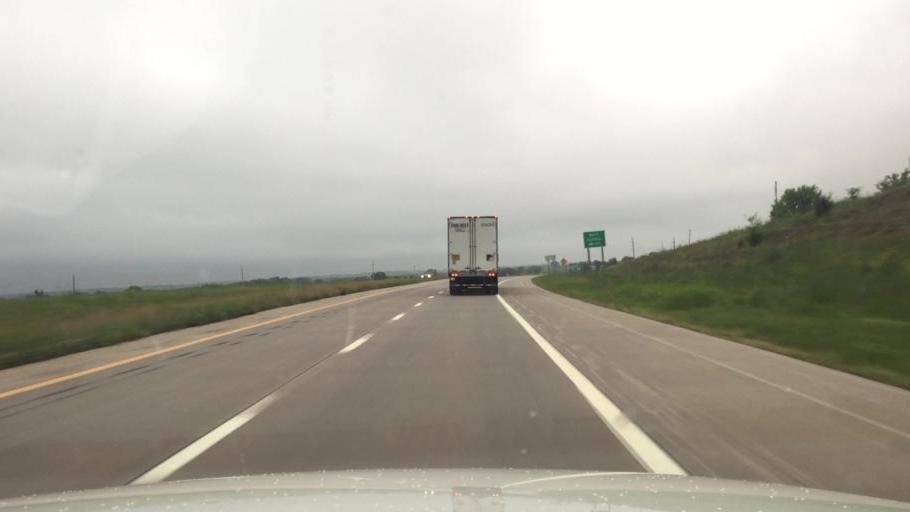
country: US
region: Kansas
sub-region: Montgomery County
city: Cherryvale
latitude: 37.2128
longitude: -95.5852
